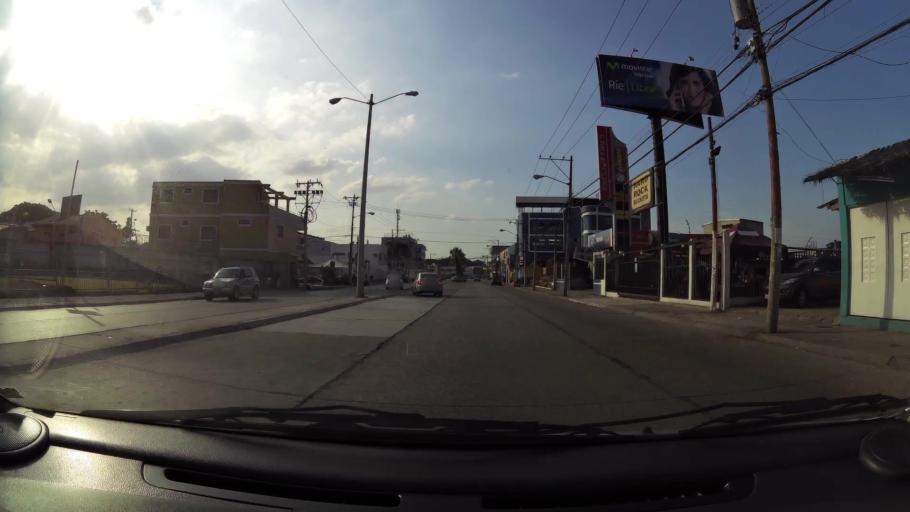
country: EC
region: Guayas
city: Guayaquil
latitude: -2.1502
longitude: -79.9057
